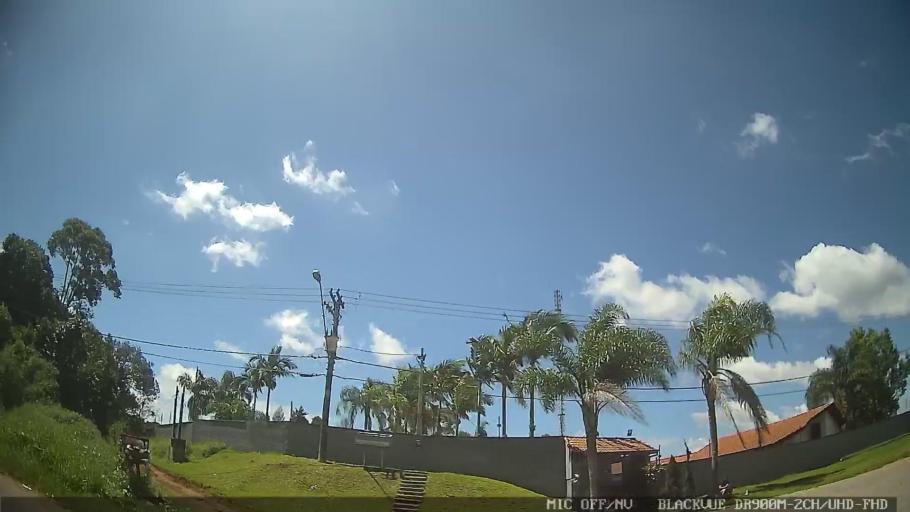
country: BR
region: Sao Paulo
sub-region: Mogi das Cruzes
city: Mogi das Cruzes
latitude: -23.6179
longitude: -46.1806
